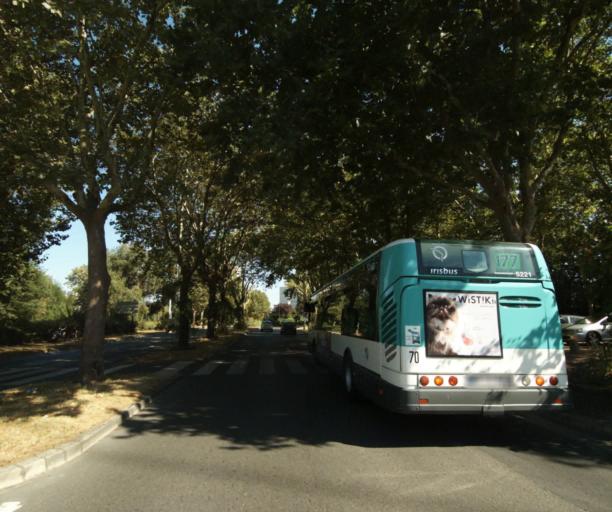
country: FR
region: Ile-de-France
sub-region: Departement des Hauts-de-Seine
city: Villeneuve-la-Garenne
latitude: 48.9411
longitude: 2.3223
